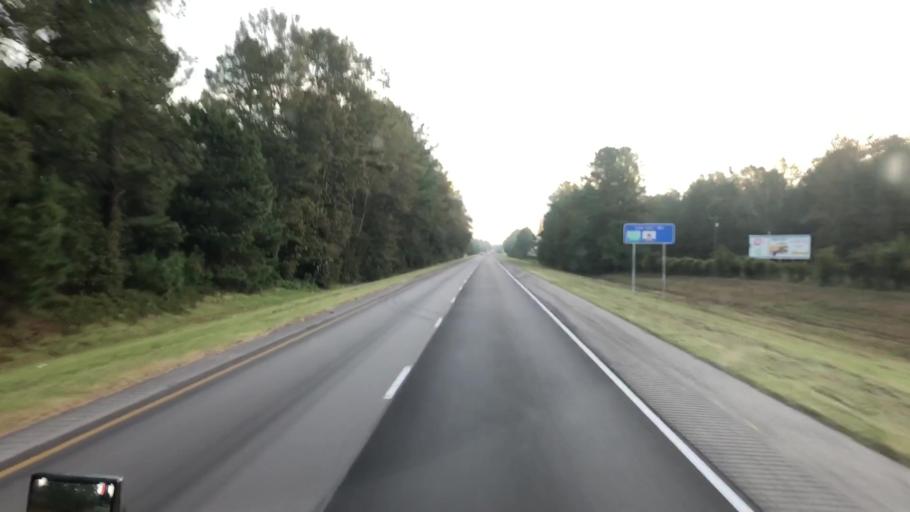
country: US
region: South Carolina
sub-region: Clarendon County
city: Manning
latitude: 33.5817
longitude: -80.3678
